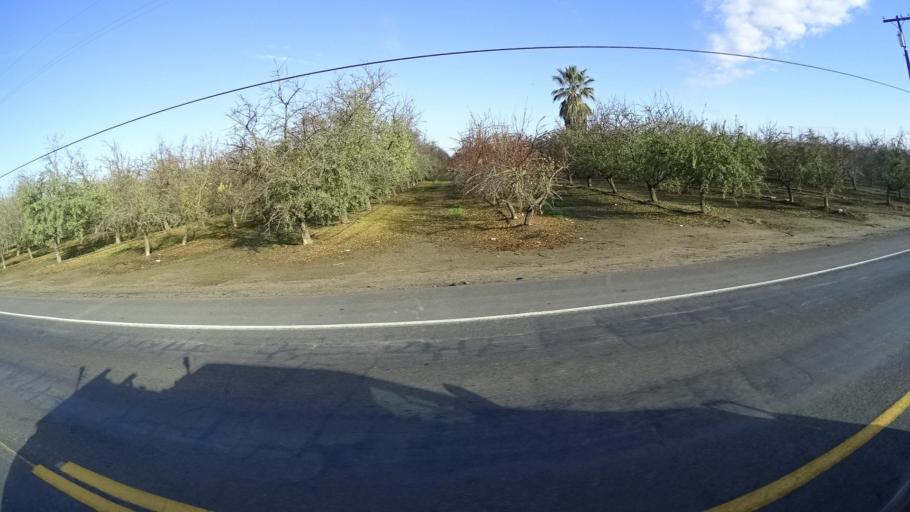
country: US
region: California
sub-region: Kern County
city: Delano
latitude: 35.7177
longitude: -119.3221
